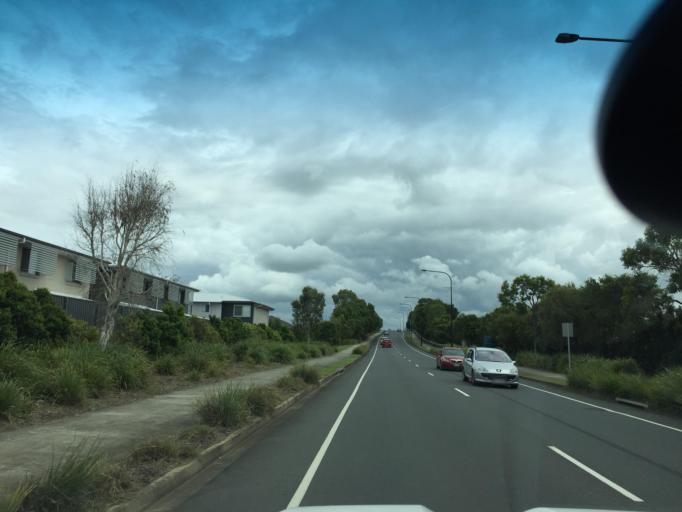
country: AU
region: Queensland
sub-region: Moreton Bay
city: Caboolture South
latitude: -27.0948
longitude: 152.9581
